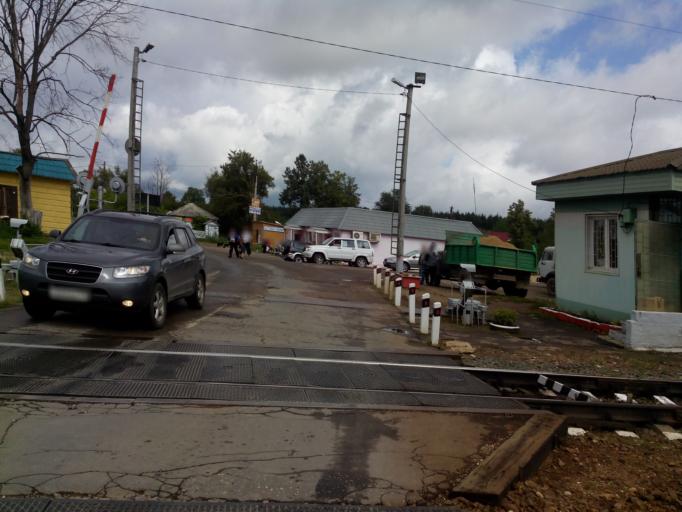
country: RU
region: Moskovskaya
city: Dorokhovo
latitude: 55.5112
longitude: 36.2174
